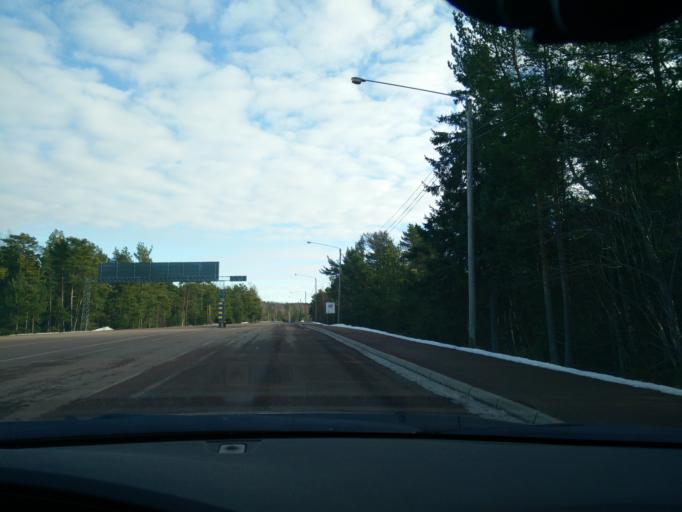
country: AX
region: Alands landsbygd
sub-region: Eckeroe
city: Eckeroe
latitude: 60.2241
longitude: 19.5393
